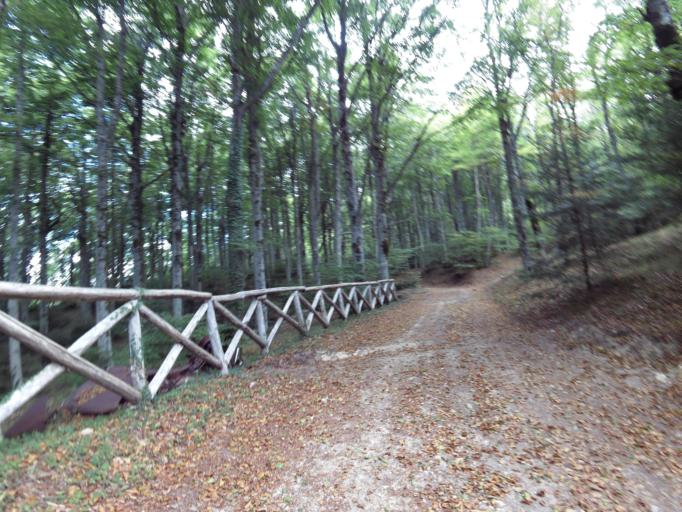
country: IT
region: Calabria
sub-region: Provincia di Vibo-Valentia
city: Mongiana
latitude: 38.5219
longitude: 16.3449
